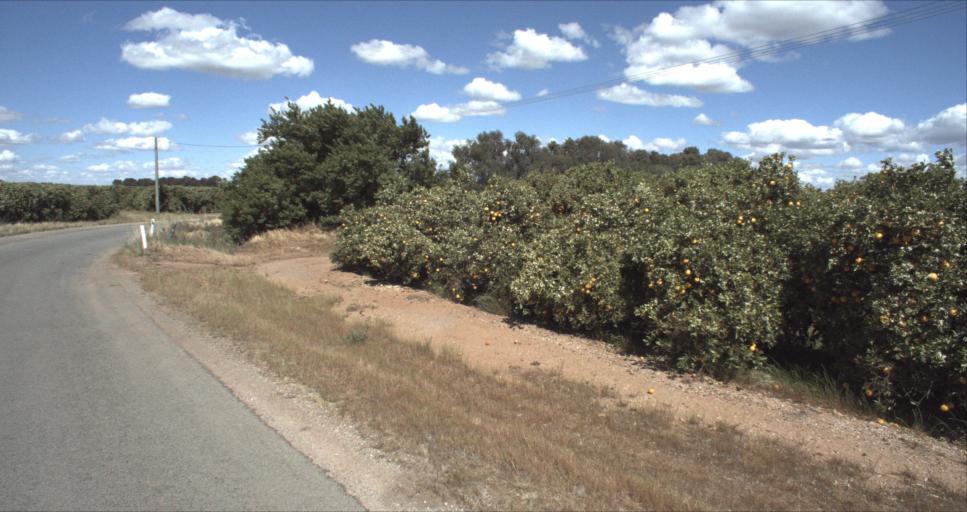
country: AU
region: New South Wales
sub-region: Leeton
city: Leeton
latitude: -34.5081
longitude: 146.2236
